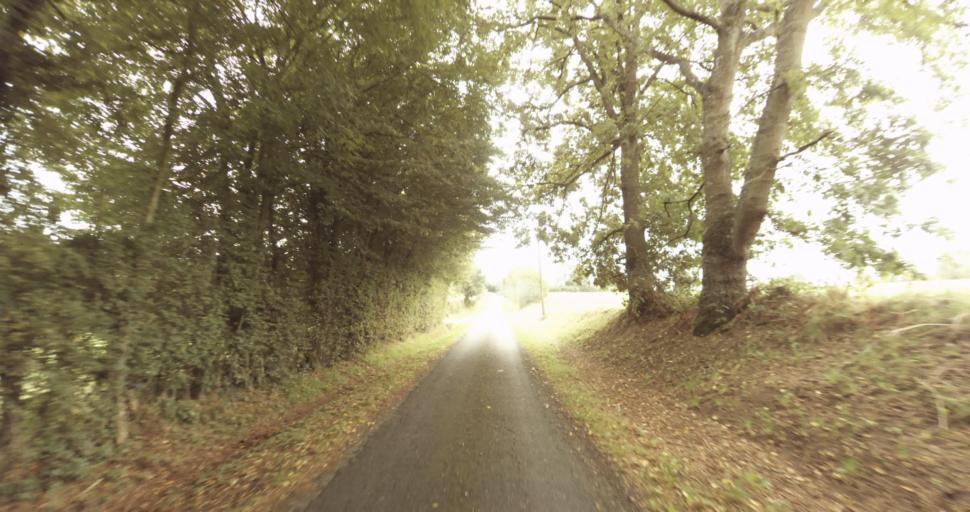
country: FR
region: Lower Normandy
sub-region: Departement de l'Orne
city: Gace
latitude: 48.6758
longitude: 0.3139
